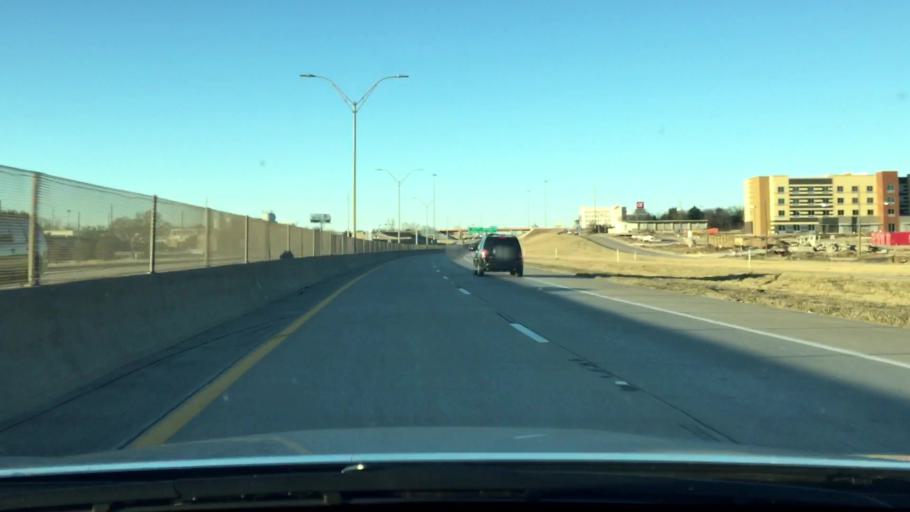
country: US
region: Texas
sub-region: Cooke County
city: Gainesville
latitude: 33.6339
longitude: -97.1552
